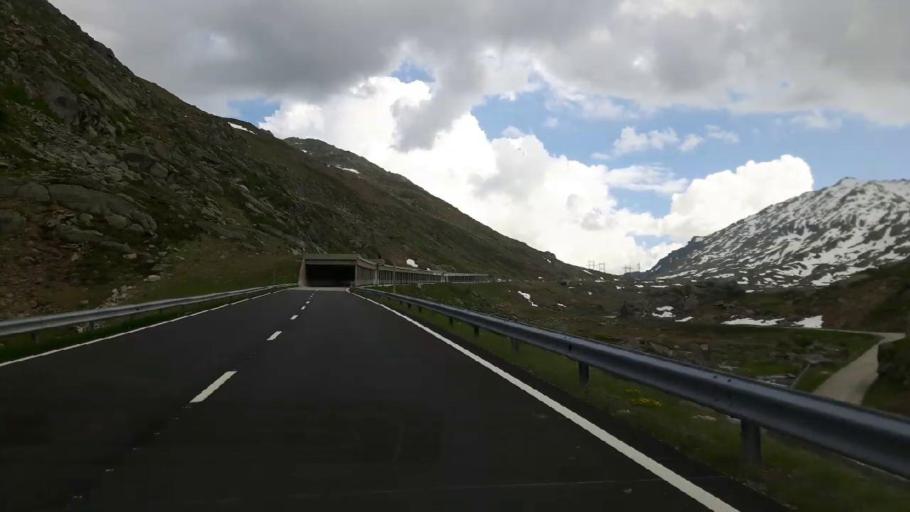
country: CH
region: Uri
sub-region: Uri
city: Andermatt
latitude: 46.5780
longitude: 8.5591
